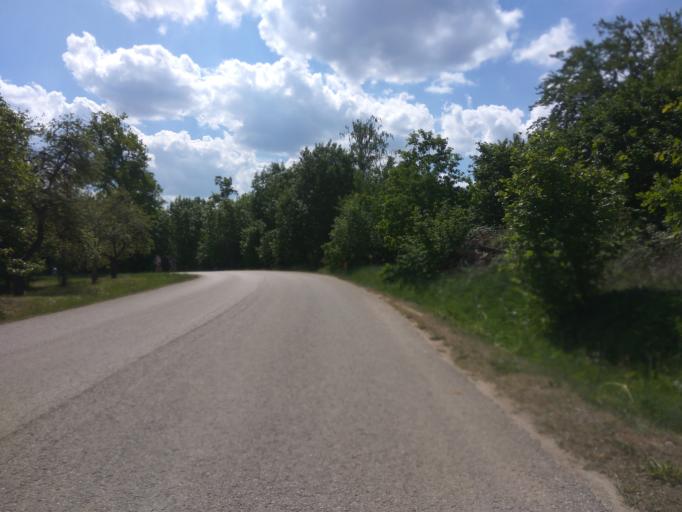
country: LV
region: Kuldigas Rajons
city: Kuldiga
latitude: 56.9161
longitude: 21.9645
